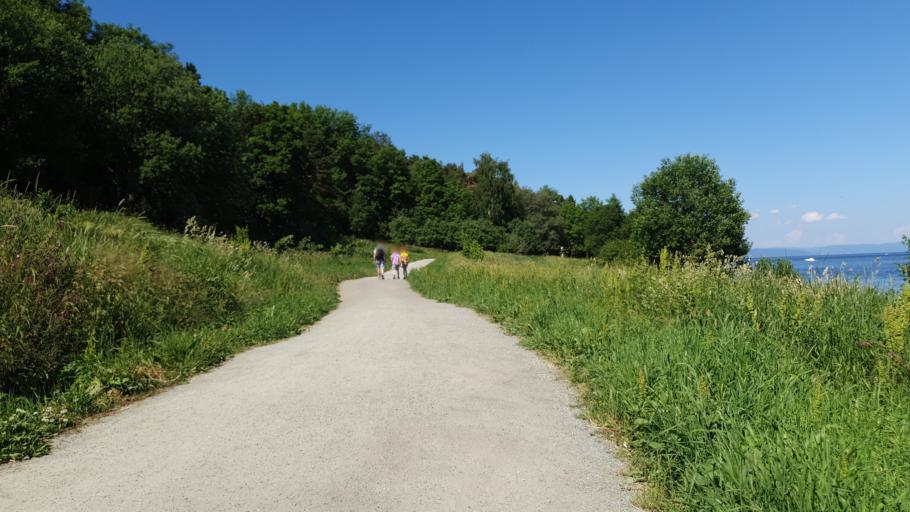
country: NO
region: Sor-Trondelag
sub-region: Trondheim
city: Trondheim
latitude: 63.4412
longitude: 10.4704
